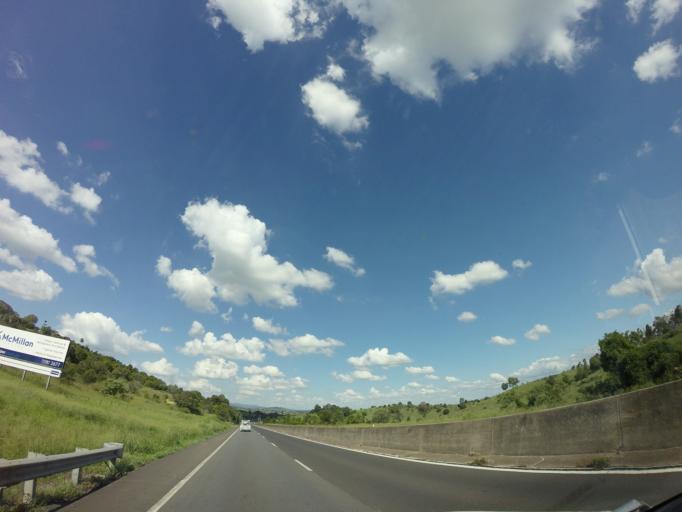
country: AU
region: Queensland
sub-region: Ipswich
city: Thagoona
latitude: -27.5650
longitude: 152.5698
